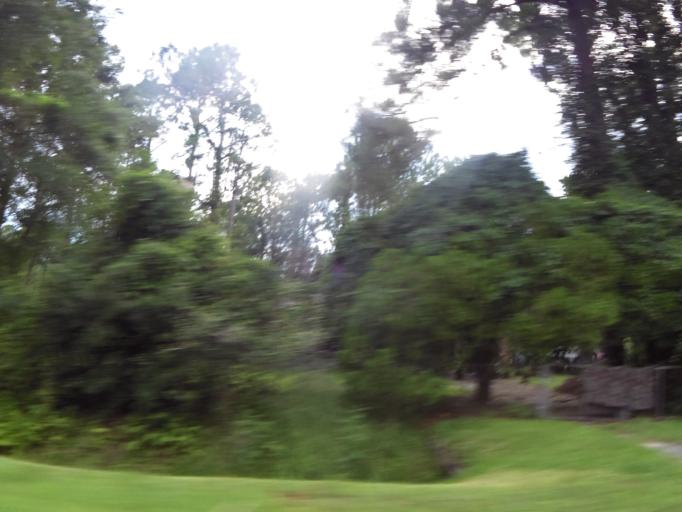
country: US
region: Florida
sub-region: Duval County
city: Jacksonville
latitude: 30.3319
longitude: -81.7899
